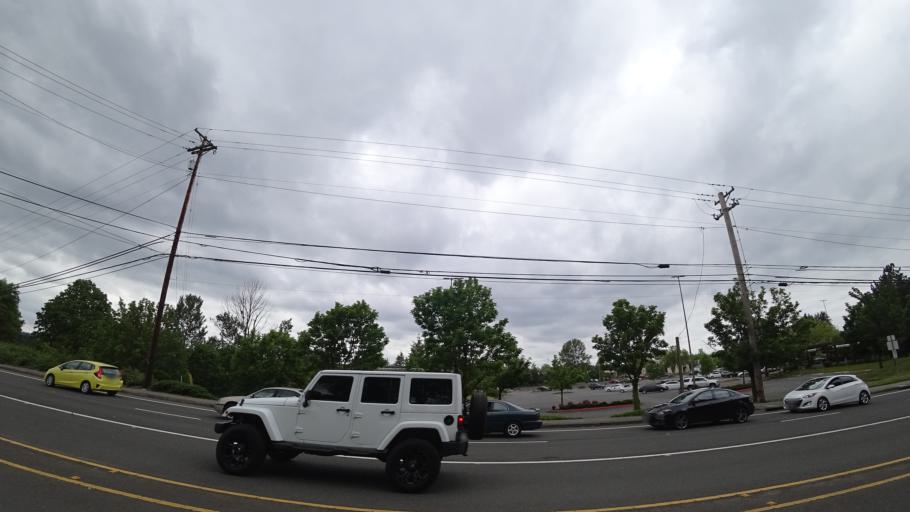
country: US
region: Oregon
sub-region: Washington County
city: Tigard
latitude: 45.4447
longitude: -122.7769
